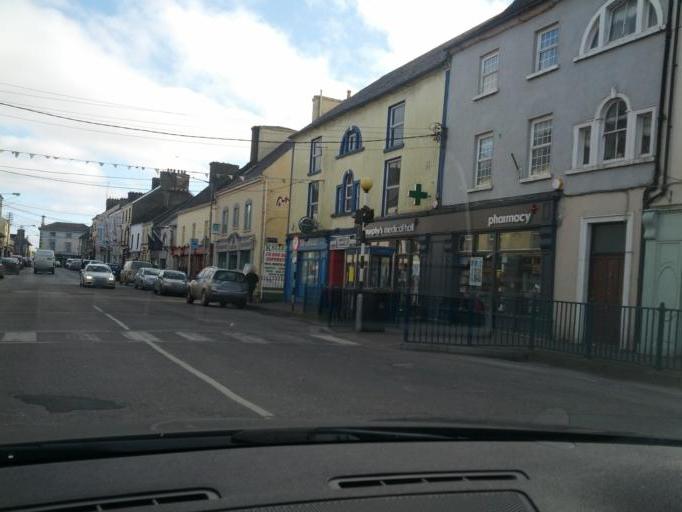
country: IE
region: Connaught
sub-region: County Galway
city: Ballinasloe
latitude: 53.3302
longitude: -8.2214
